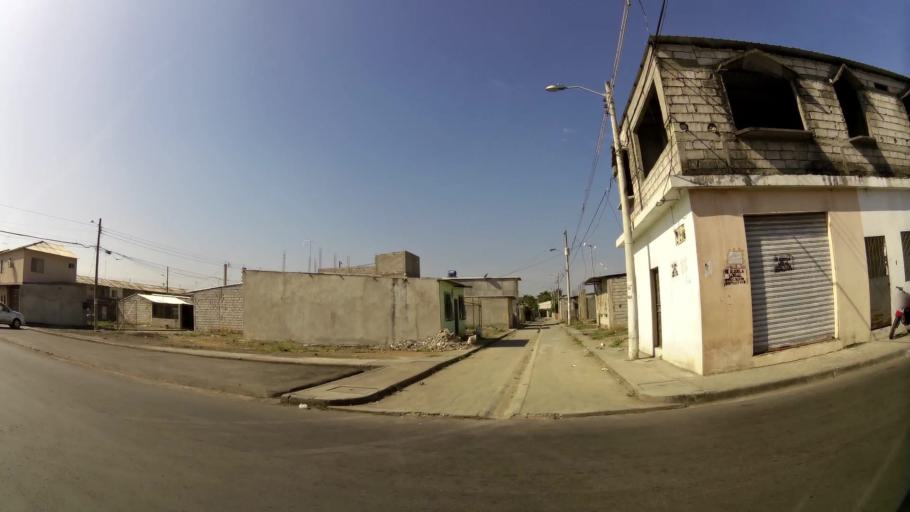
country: EC
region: Guayas
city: Eloy Alfaro
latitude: -2.0987
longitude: -79.9203
